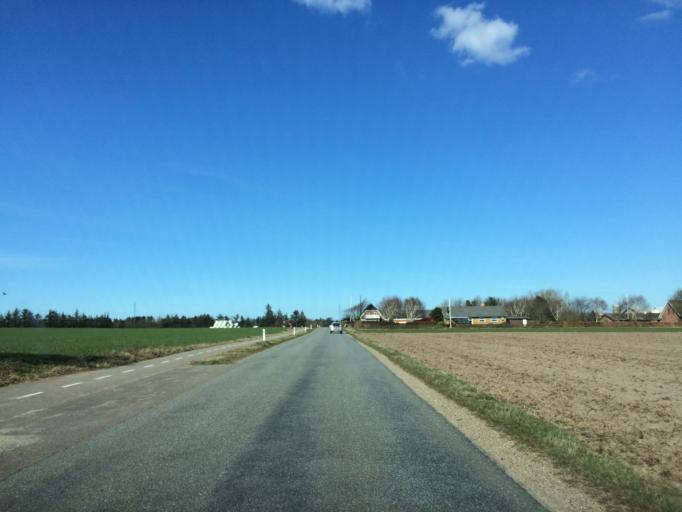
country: DK
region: South Denmark
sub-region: Varde Kommune
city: Oksbol
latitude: 55.7273
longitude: 8.2673
